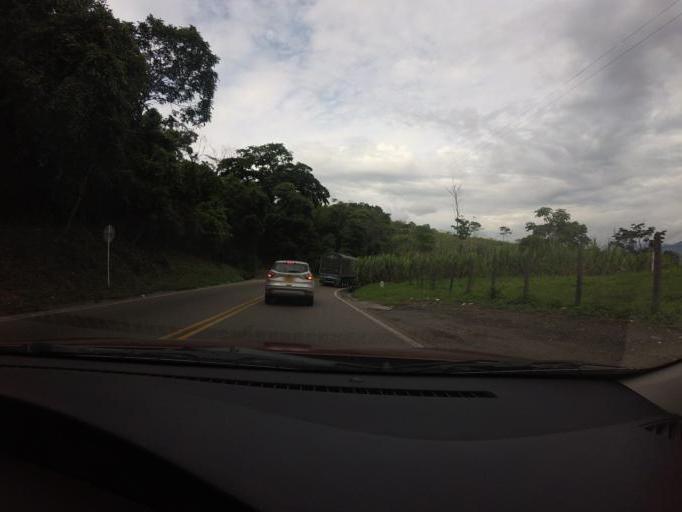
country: CO
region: Cundinamarca
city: Villeta
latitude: 5.0228
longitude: -74.5123
